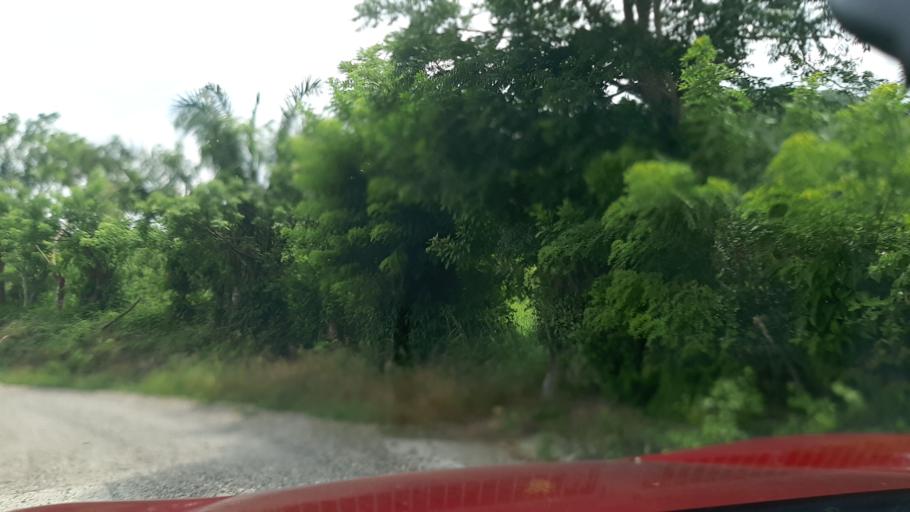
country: MX
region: Veracruz
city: Gutierrez Zamora
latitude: 20.4516
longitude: -97.1767
